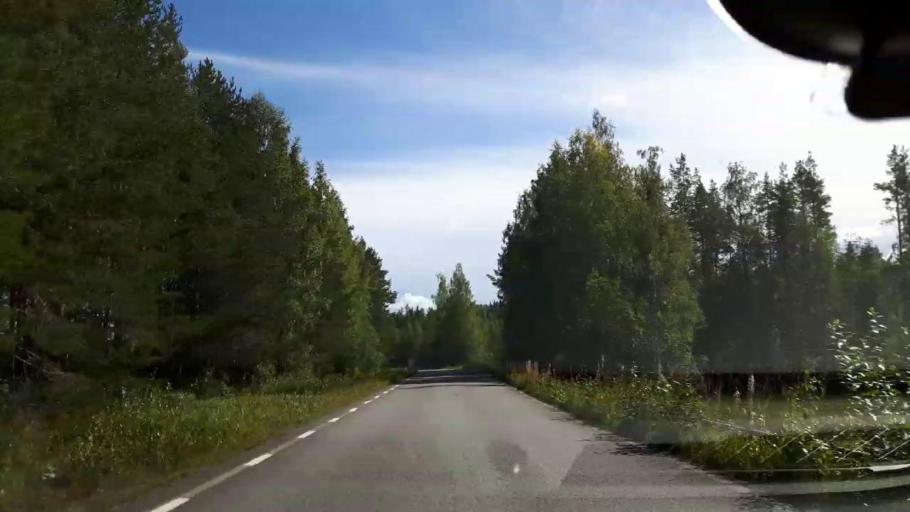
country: SE
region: Jaemtland
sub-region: OEstersunds Kommun
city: Lit
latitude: 63.2263
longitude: 15.2818
